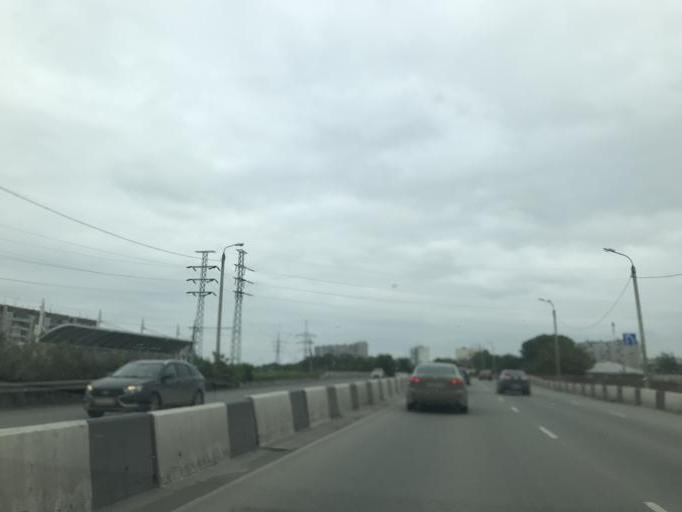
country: RU
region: Chelyabinsk
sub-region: Gorod Chelyabinsk
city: Chelyabinsk
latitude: 55.1671
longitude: 61.4286
